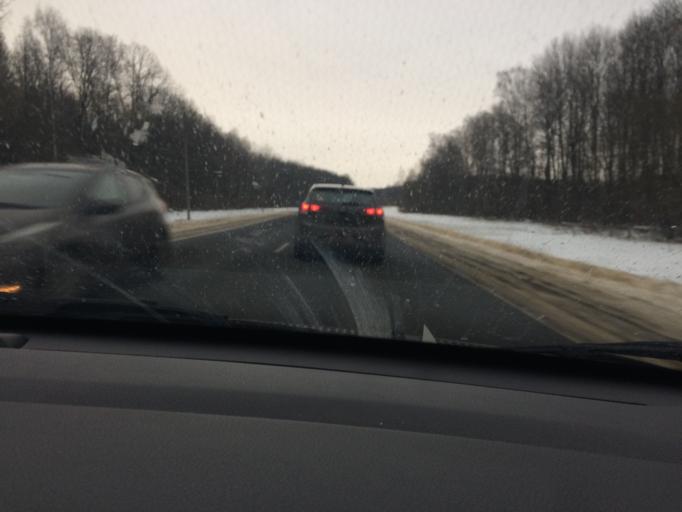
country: RU
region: Tula
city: Venev
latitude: 54.3372
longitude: 38.1212
